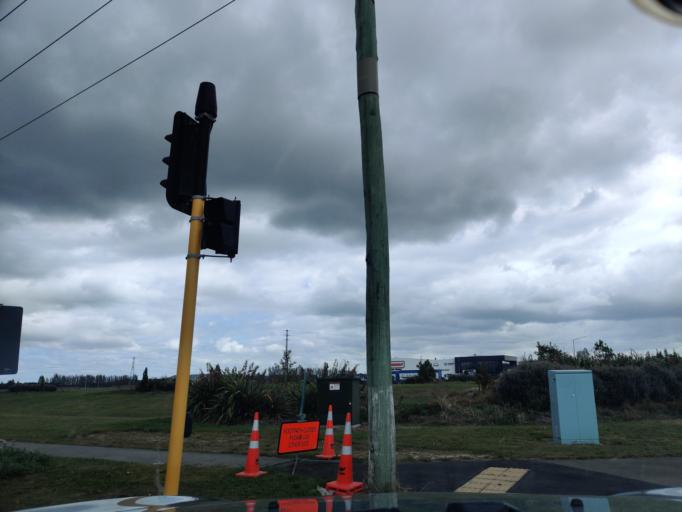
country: NZ
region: Canterbury
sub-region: Selwyn District
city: Prebbleton
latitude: -43.5557
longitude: 172.5120
